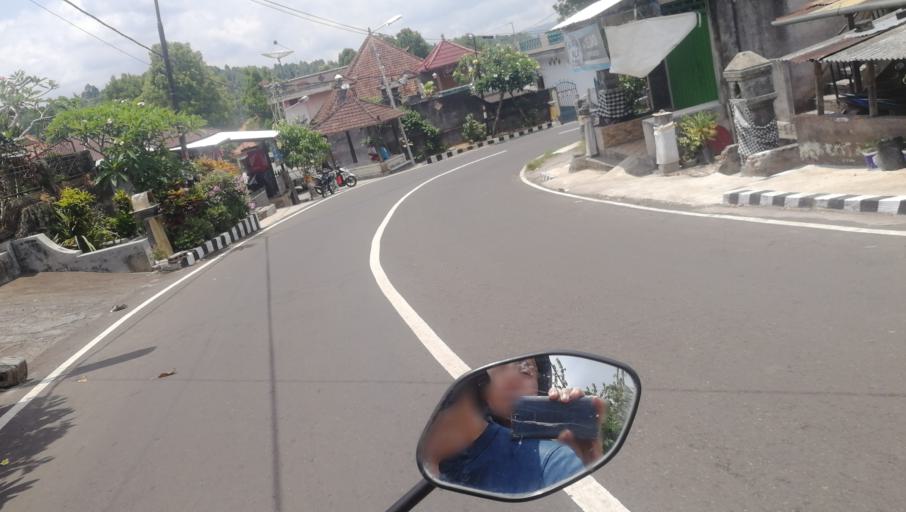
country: ID
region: Bali
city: Banjar Pedawa
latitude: -8.2640
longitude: 115.0342
